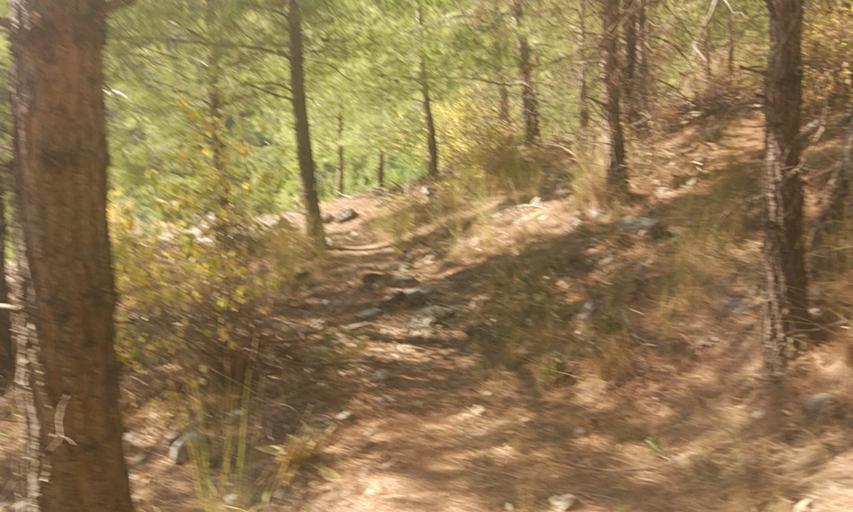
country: TR
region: Antalya
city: Tekirova
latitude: 36.4882
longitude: 30.4248
